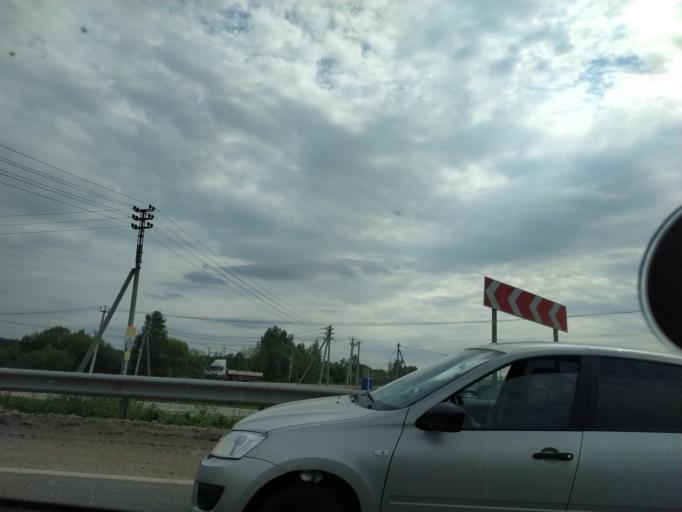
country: RU
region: Moskovskaya
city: Malyshevo
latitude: 55.4868
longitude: 38.3244
